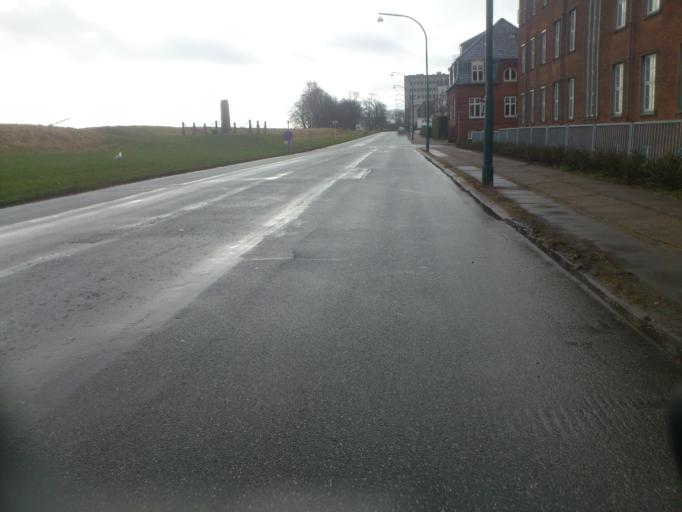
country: DK
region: South Denmark
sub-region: Fredericia Kommune
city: Fredericia
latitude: 55.5661
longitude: 9.7676
